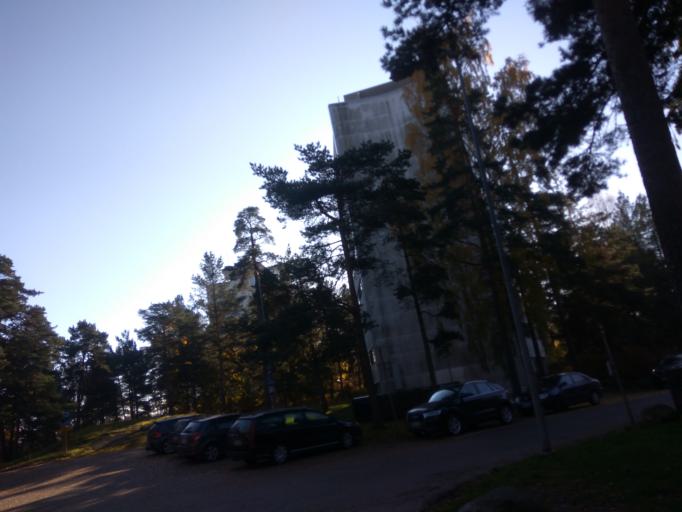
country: FI
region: Uusimaa
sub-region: Helsinki
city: Otaniemi
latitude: 60.1770
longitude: 24.7951
